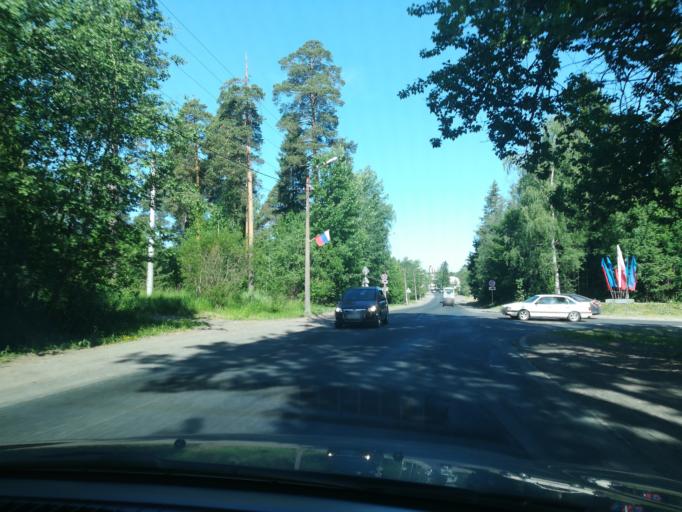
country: RU
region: Leningrad
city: Svetogorsk
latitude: 61.1041
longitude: 28.8685
